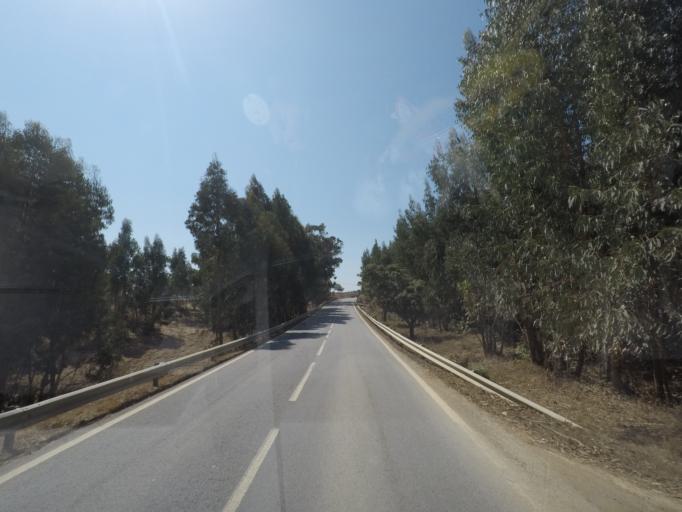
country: PT
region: Beja
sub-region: Odemira
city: Sao Teotonio
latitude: 37.5430
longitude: -8.6882
